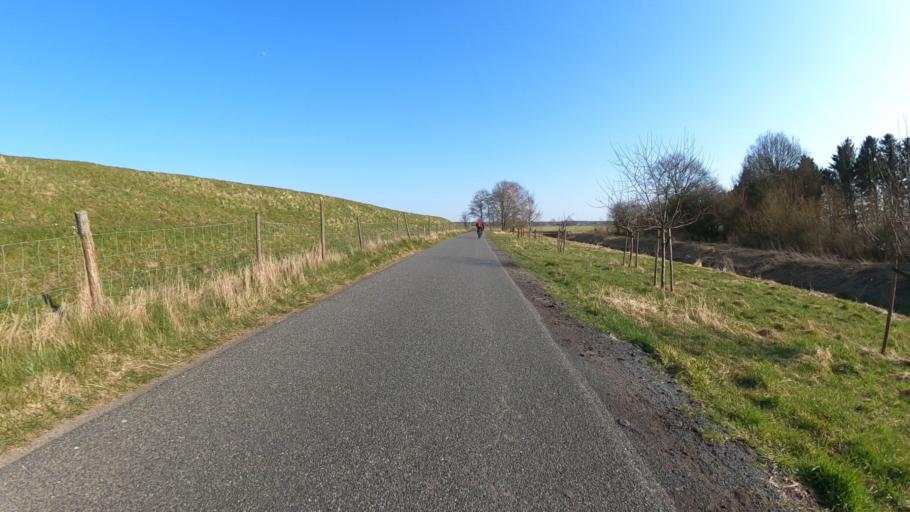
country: DE
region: Schleswig-Holstein
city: Seester
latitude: 53.7362
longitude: 9.6127
